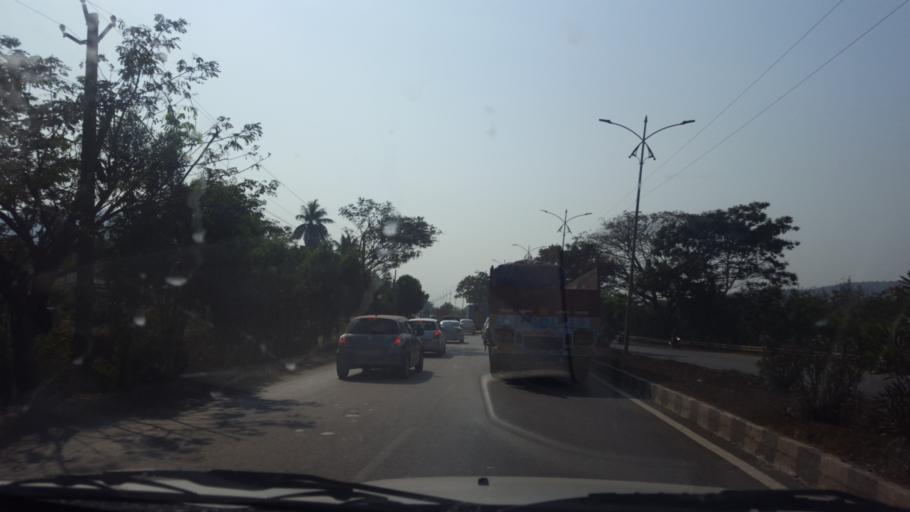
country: IN
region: Andhra Pradesh
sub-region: Vishakhapatnam
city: Anakapalle
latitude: 17.6873
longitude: 83.0892
